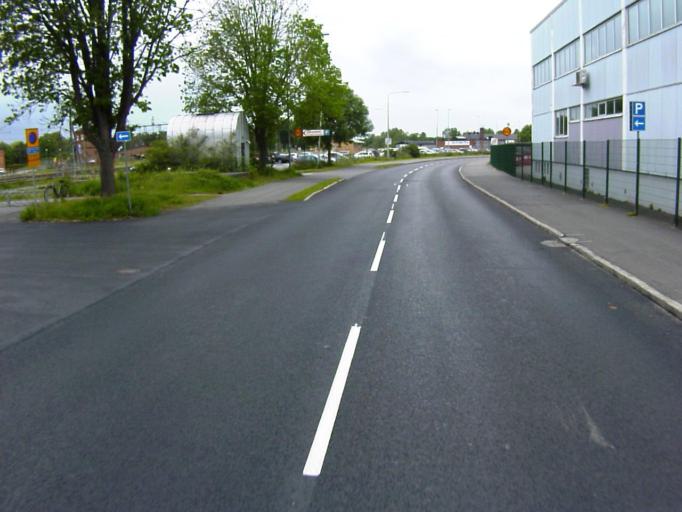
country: SE
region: Skane
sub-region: Kristianstads Kommun
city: Kristianstad
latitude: 56.0335
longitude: 14.1505
